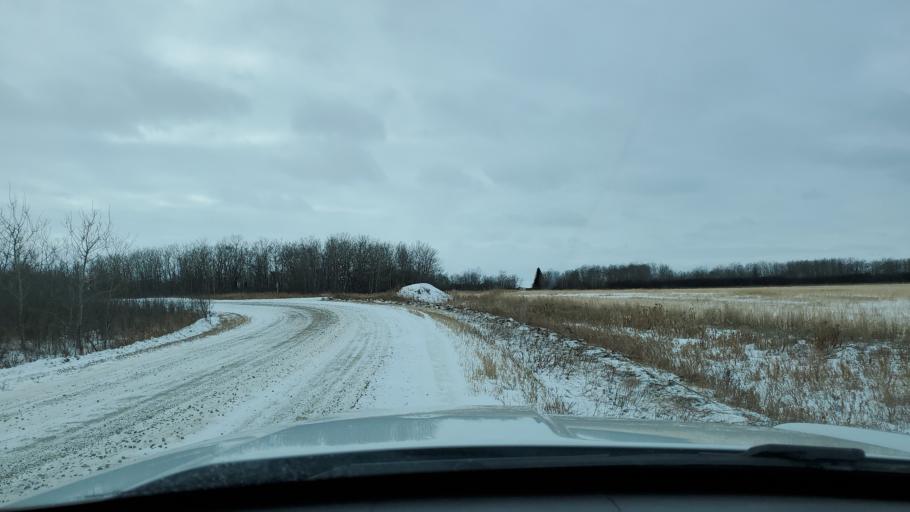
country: CA
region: Saskatchewan
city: White City
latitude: 50.7696
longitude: -104.1535
